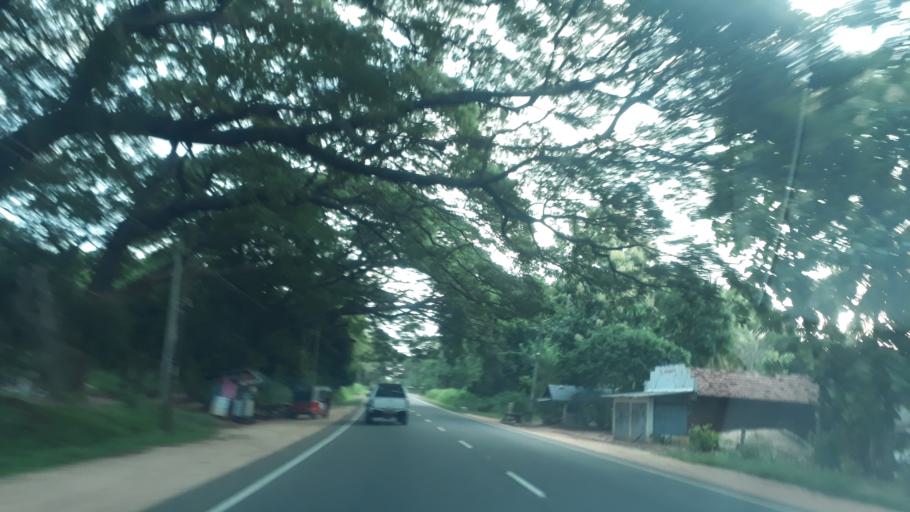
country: LK
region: Central
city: Sigiriya
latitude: 7.9794
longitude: 80.7172
